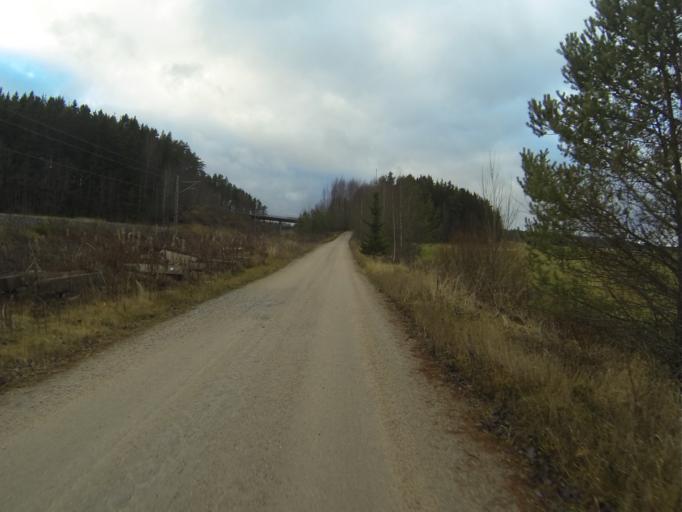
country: FI
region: Varsinais-Suomi
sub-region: Salo
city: Halikko
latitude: 60.4035
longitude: 23.0063
